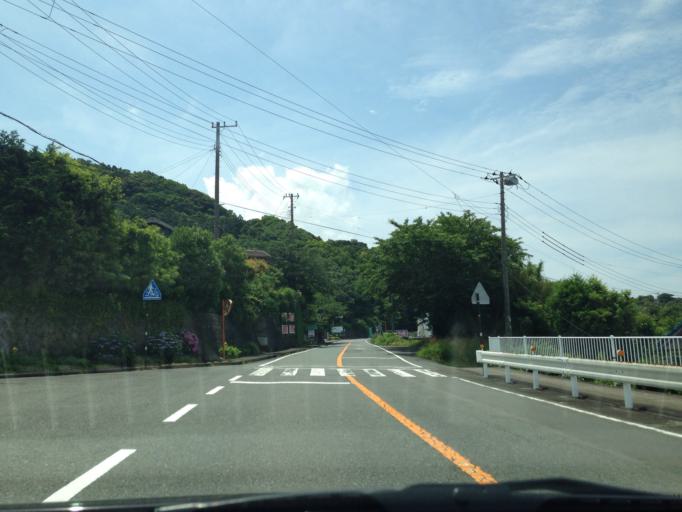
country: JP
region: Shizuoka
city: Heda
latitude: 34.8845
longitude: 138.7636
